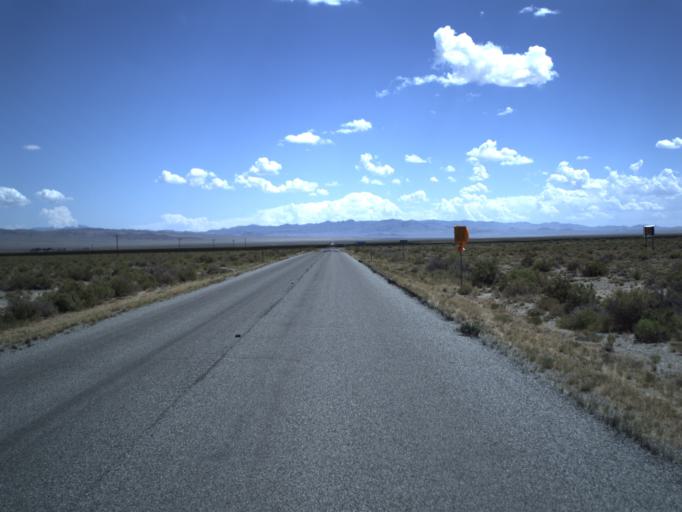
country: US
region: Nevada
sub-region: White Pine County
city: McGill
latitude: 39.0569
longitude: -114.0458
